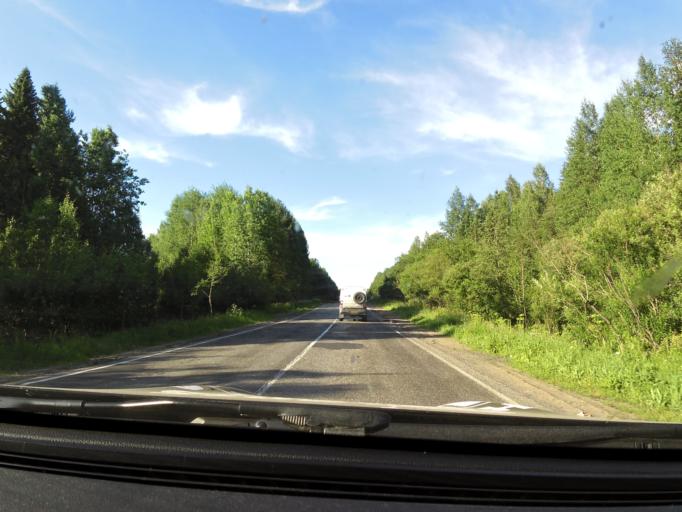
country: RU
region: Kirov
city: Belorechensk
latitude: 58.7742
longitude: 52.3745
